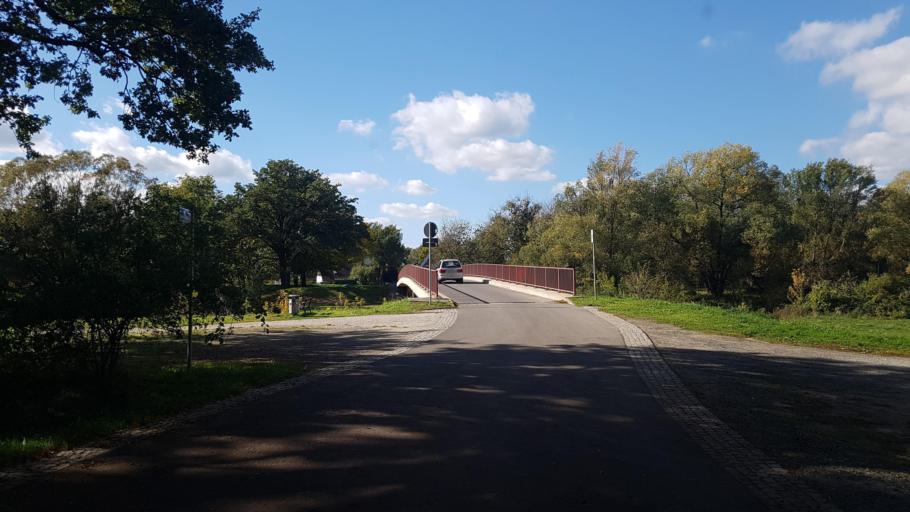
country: DE
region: Brandenburg
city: Cottbus
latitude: 51.8057
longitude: 14.3605
